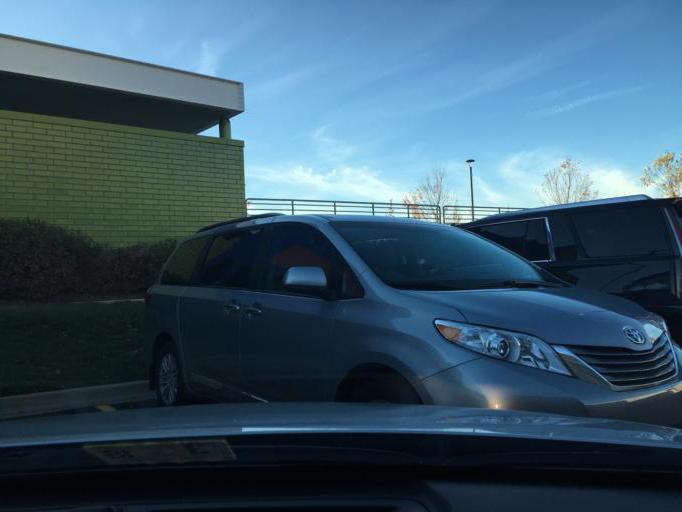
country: US
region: Michigan
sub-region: Oakland County
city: Clawson
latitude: 42.5631
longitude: -83.1525
